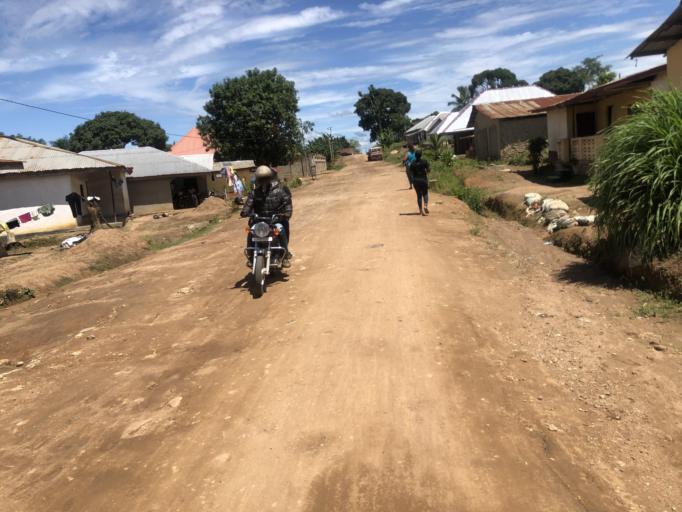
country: SL
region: Eastern Province
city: Koidu
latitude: 8.6415
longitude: -10.9572
